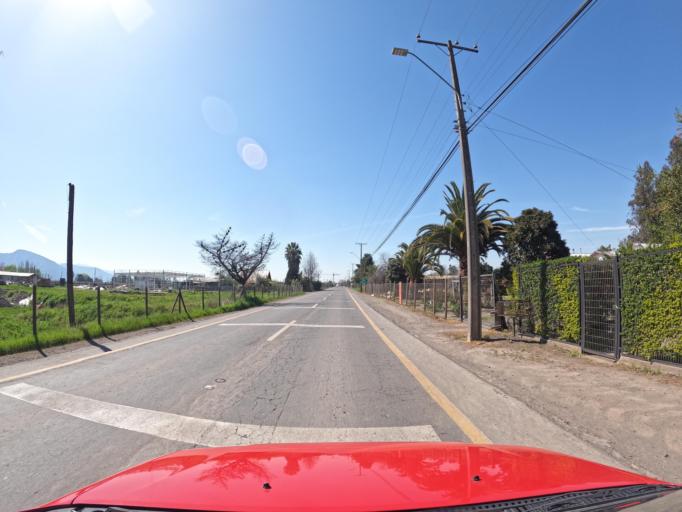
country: CL
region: Maule
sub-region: Provincia de Curico
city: Rauco
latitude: -35.0027
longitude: -71.3973
